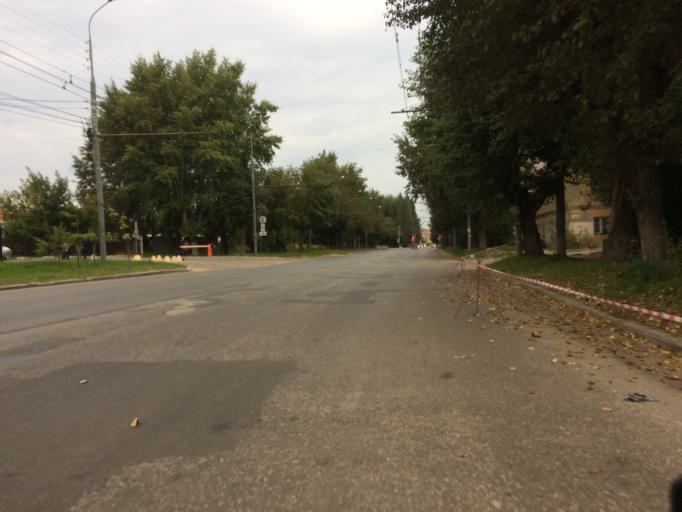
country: RU
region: Mariy-El
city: Yoshkar-Ola
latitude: 56.6351
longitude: 47.8664
